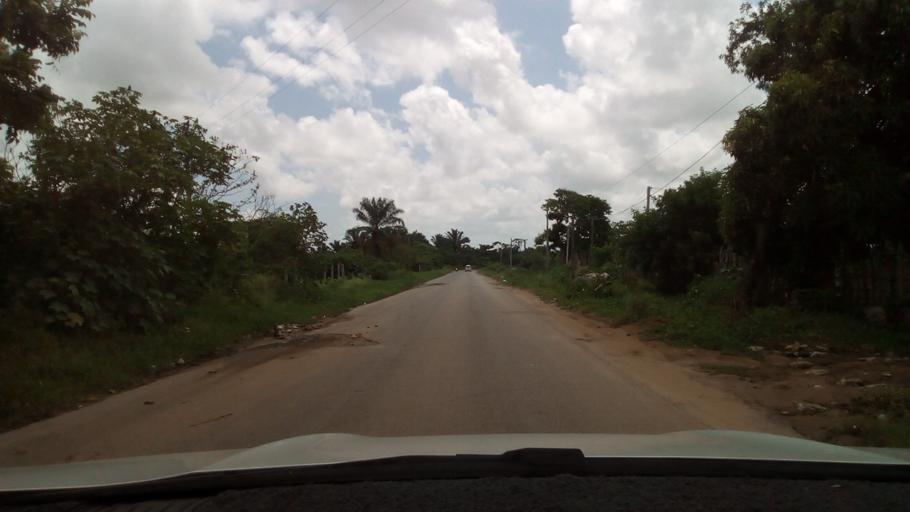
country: BR
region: Paraiba
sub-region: Alhandra
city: Alhandra
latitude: -7.4421
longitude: -34.9120
